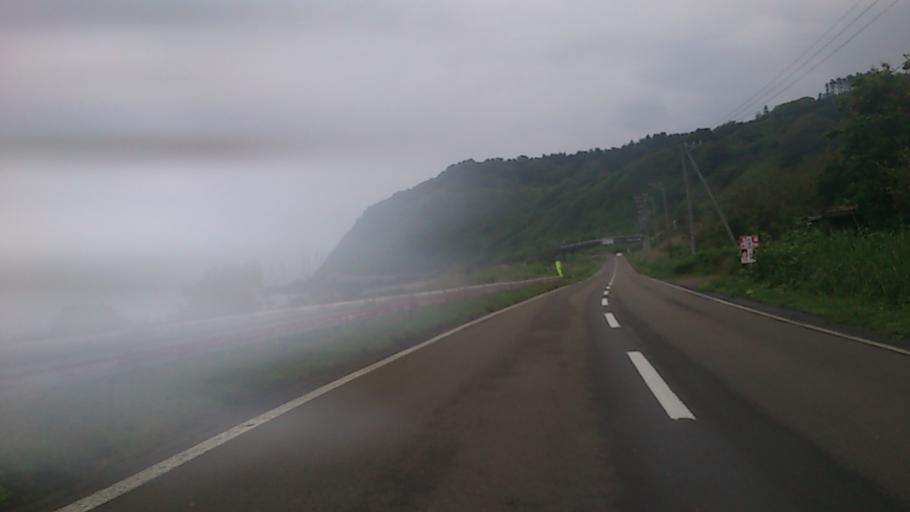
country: JP
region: Akita
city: Noshiromachi
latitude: 40.4741
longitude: 139.9470
